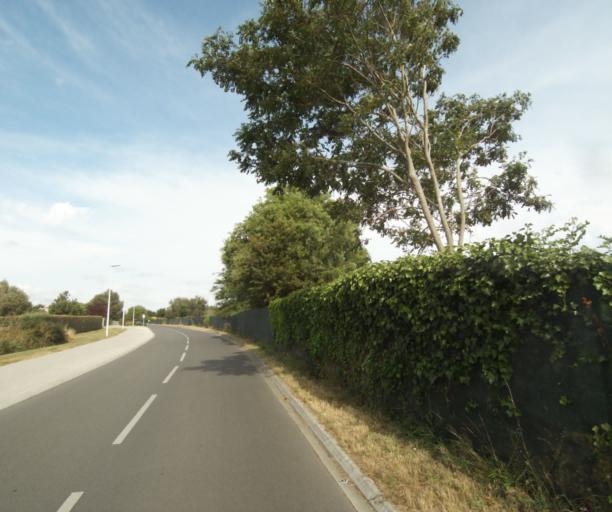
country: FR
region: Pays de la Loire
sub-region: Departement de la Vendee
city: Chateau-d'Olonne
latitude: 46.4788
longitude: -1.7353
